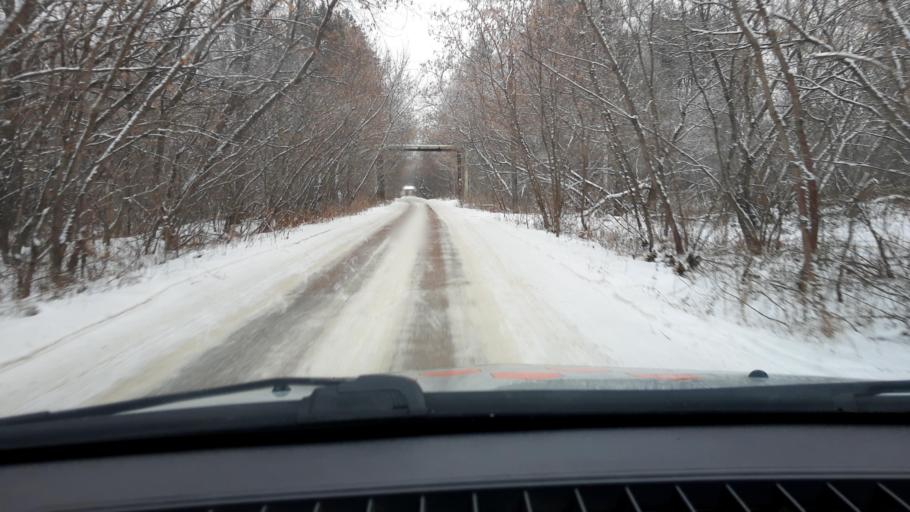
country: RU
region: Bashkortostan
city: Iglino
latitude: 54.8195
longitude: 56.1922
